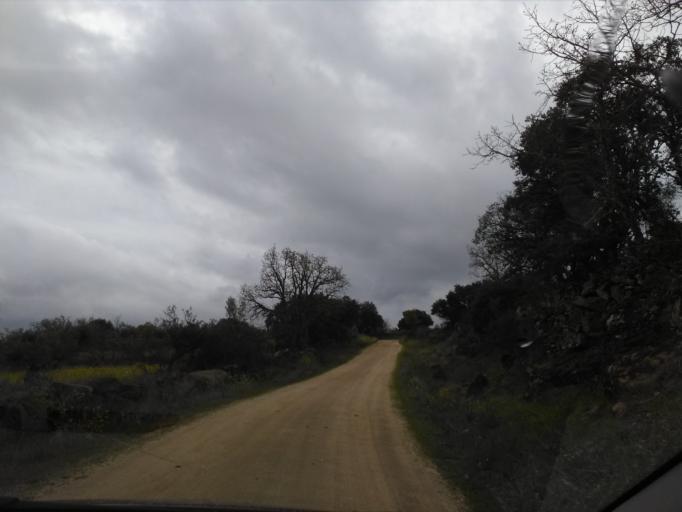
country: ES
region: Castille and Leon
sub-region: Provincia de Salamanca
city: Puerto Seguro
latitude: 40.8360
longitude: -6.7365
